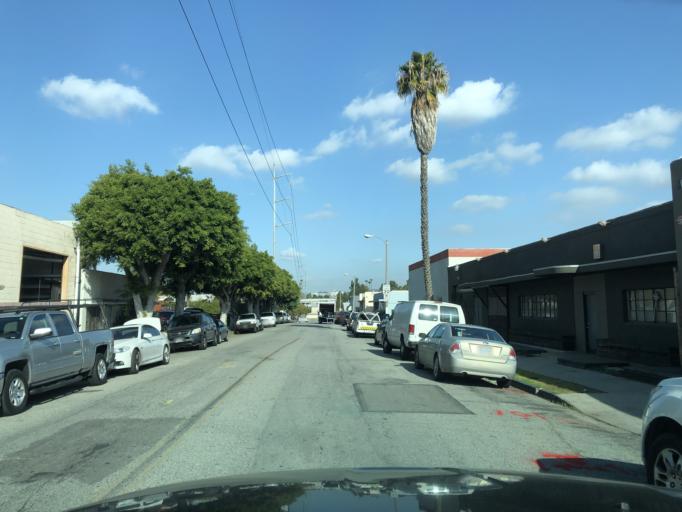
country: US
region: California
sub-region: Los Angeles County
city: Inglewood
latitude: 33.9647
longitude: -118.3687
